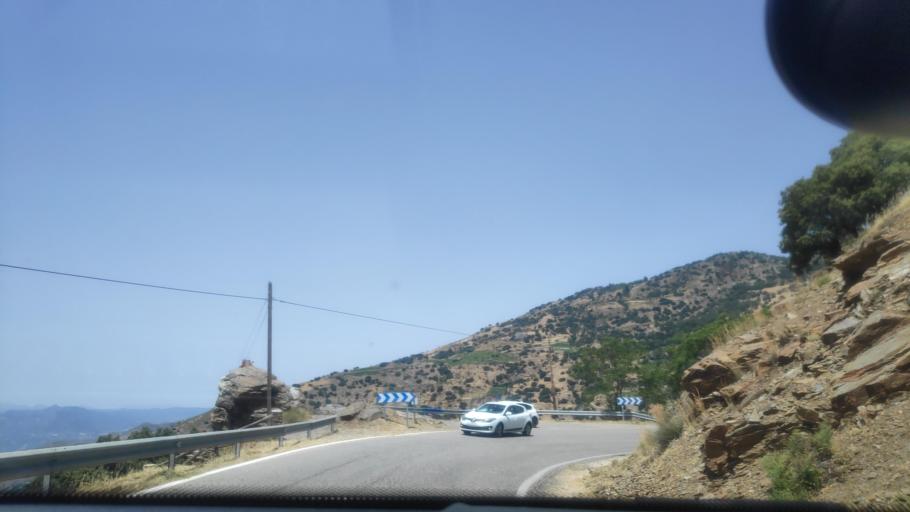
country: ES
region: Andalusia
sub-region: Provincia de Granada
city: Pampaneira
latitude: 36.9270
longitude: -3.3659
